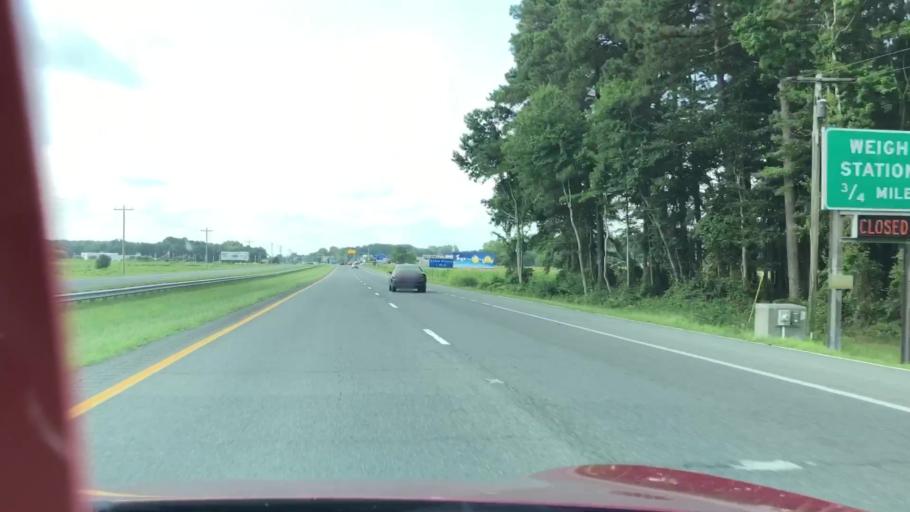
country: US
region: Maryland
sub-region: Wicomico County
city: Delmar
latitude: 38.4355
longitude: -75.5630
